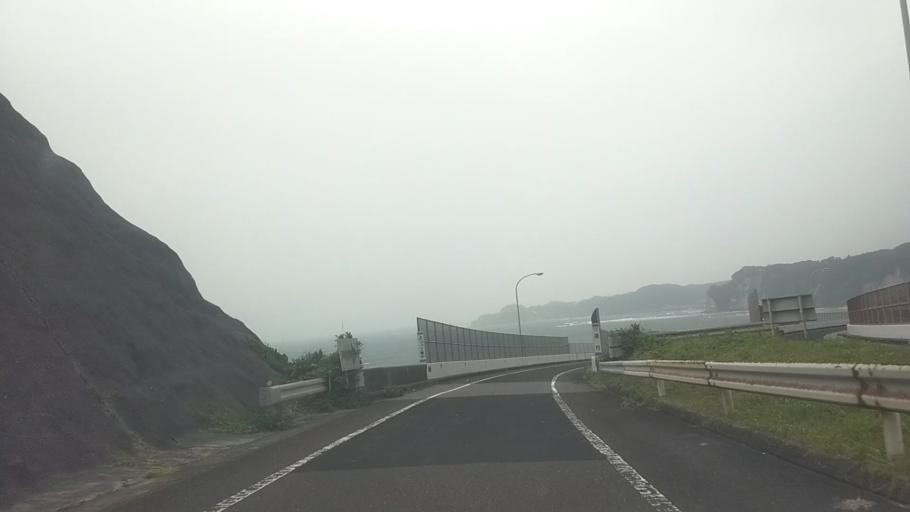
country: JP
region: Chiba
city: Katsuura
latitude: 35.1524
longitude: 140.3050
